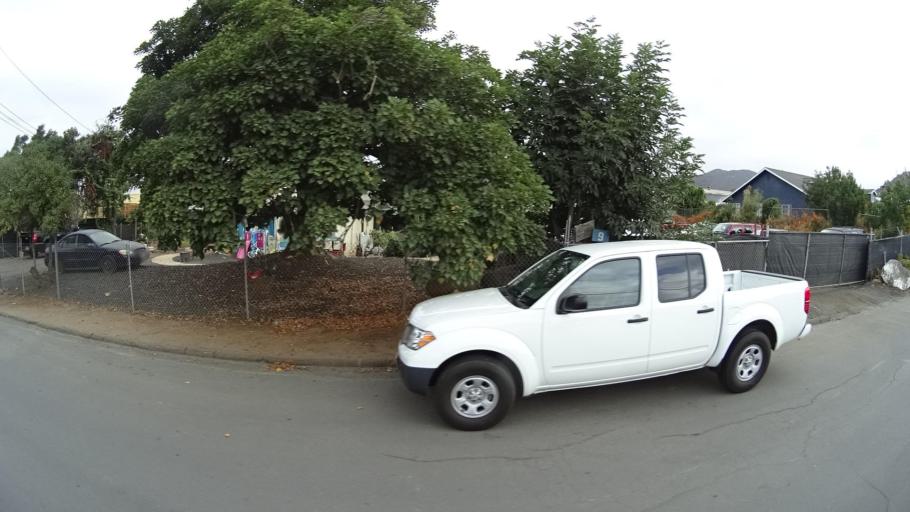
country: US
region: California
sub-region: San Diego County
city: Vista
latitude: 33.2120
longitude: -117.2067
